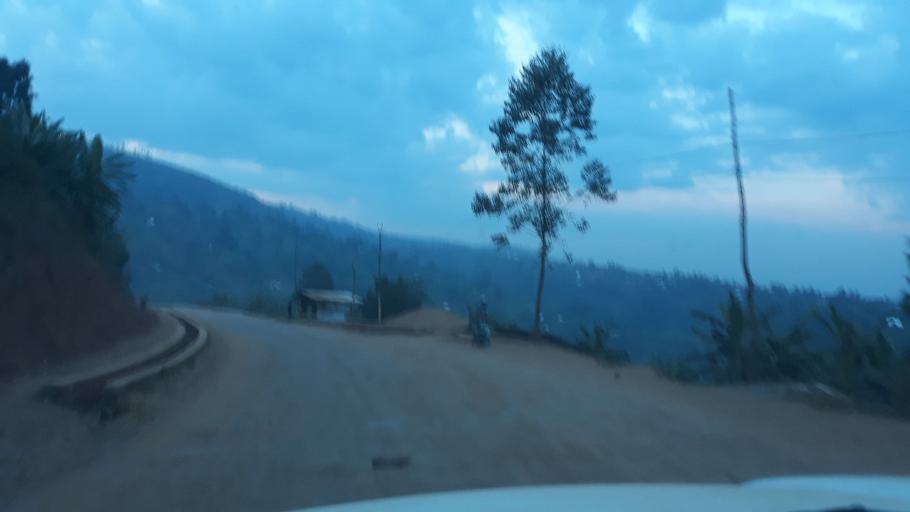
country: CD
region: South Kivu
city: Bukavu
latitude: -2.5642
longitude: 28.8611
